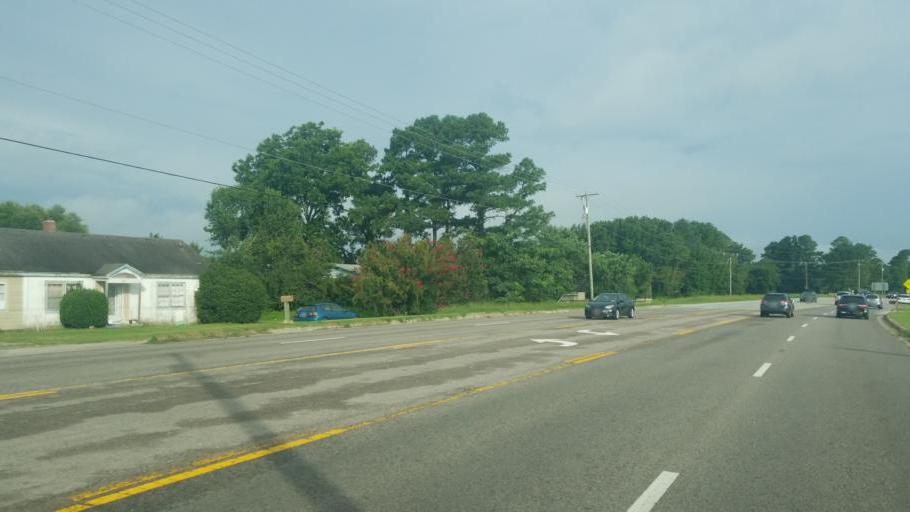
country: US
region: North Carolina
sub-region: Currituck County
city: Currituck
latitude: 36.3871
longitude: -75.9769
